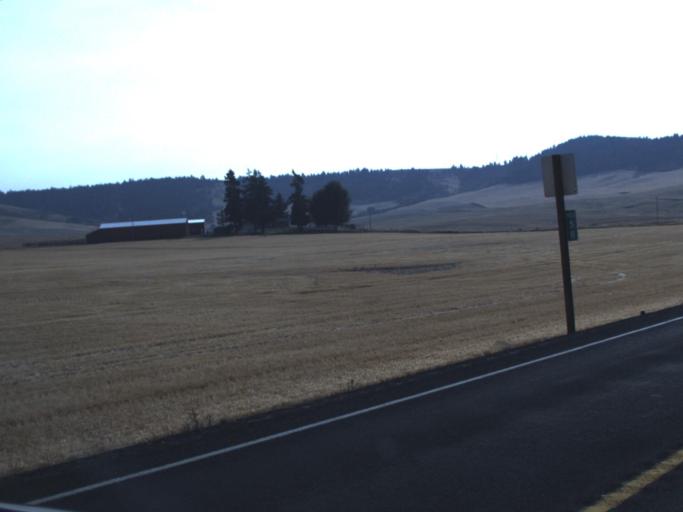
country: US
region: Idaho
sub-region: Benewah County
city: Plummer
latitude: 47.3149
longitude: -117.1691
